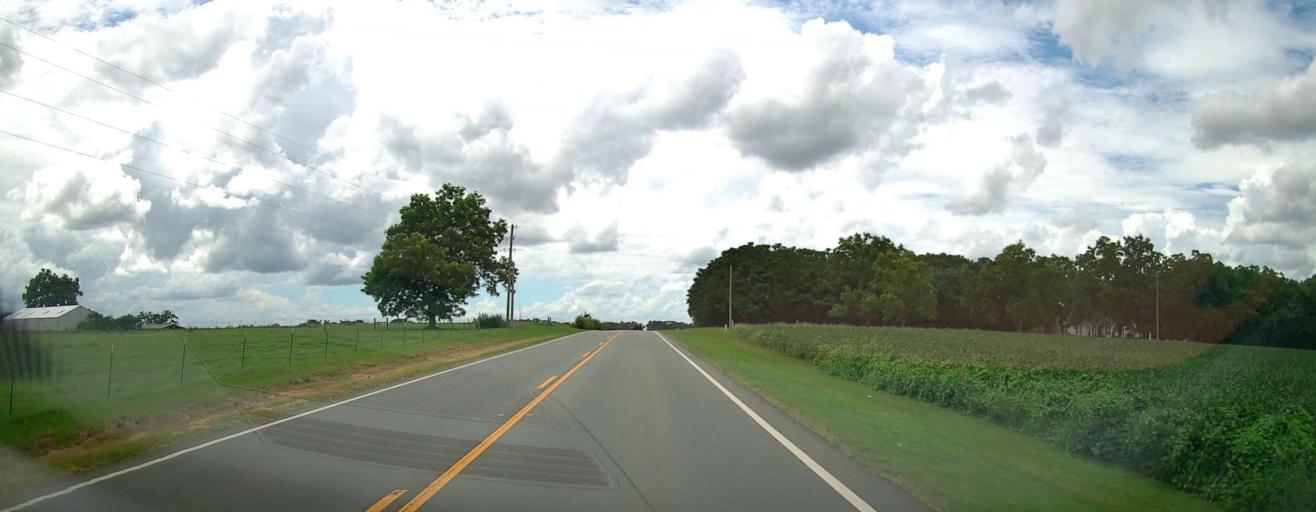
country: US
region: Georgia
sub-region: Macon County
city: Montezuma
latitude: 32.2931
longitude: -83.9808
